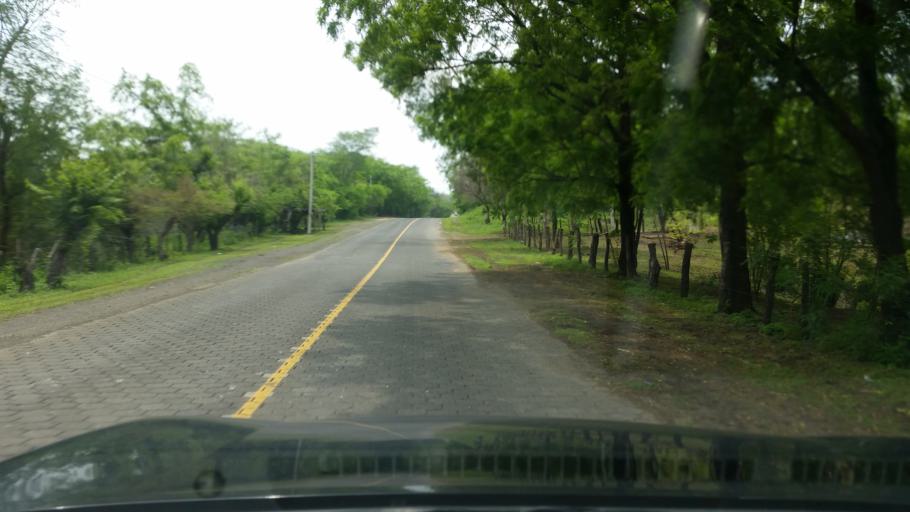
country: NI
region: Managua
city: Carlos Fonseca Amador
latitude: 11.9313
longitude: -86.5069
